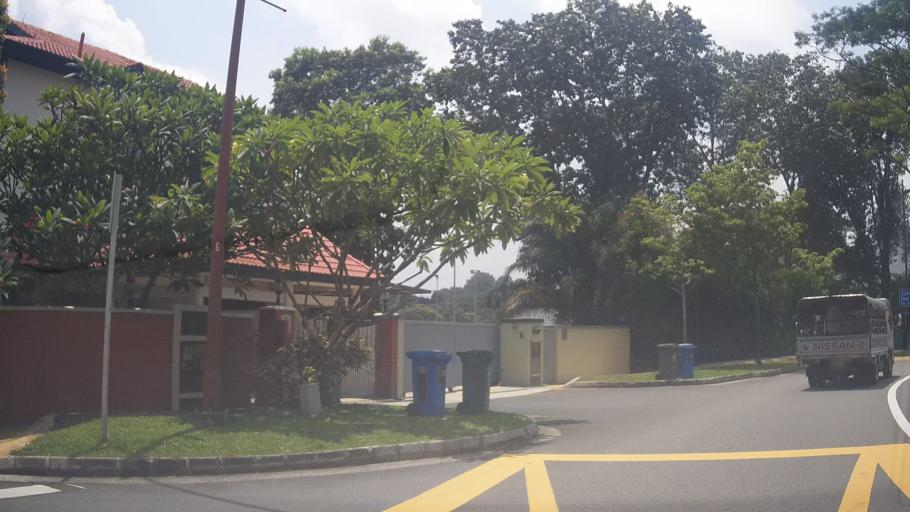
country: SG
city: Singapore
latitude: 1.3150
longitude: 103.7846
